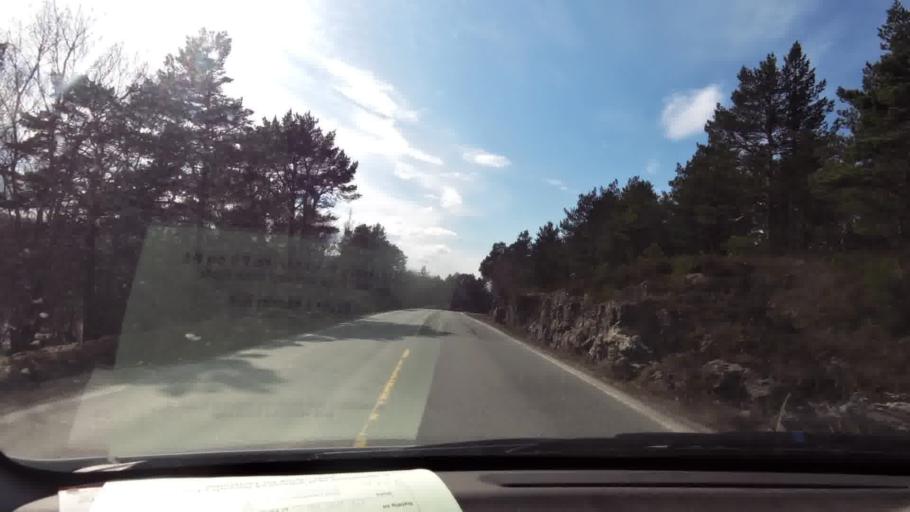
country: NO
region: More og Romsdal
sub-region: Kristiansund
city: Rensvik
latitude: 63.1079
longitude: 7.8322
